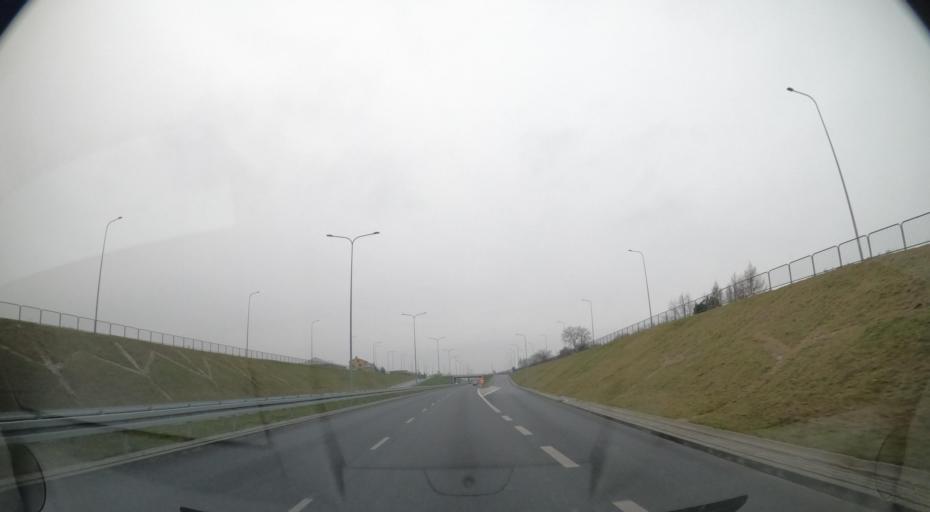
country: PL
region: Masovian Voivodeship
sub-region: Radom
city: Radom
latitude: 51.3995
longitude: 21.1988
